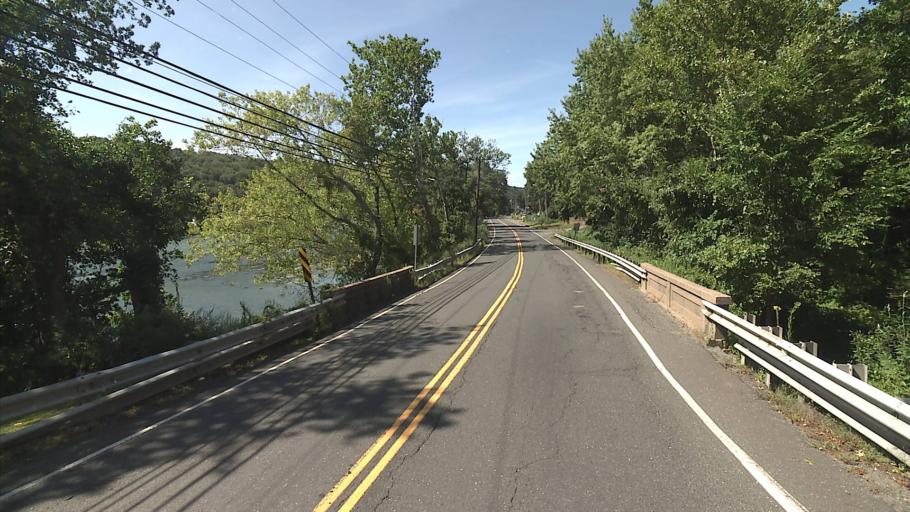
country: US
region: Connecticut
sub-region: New Haven County
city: Ansonia
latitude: 41.3642
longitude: -73.1402
